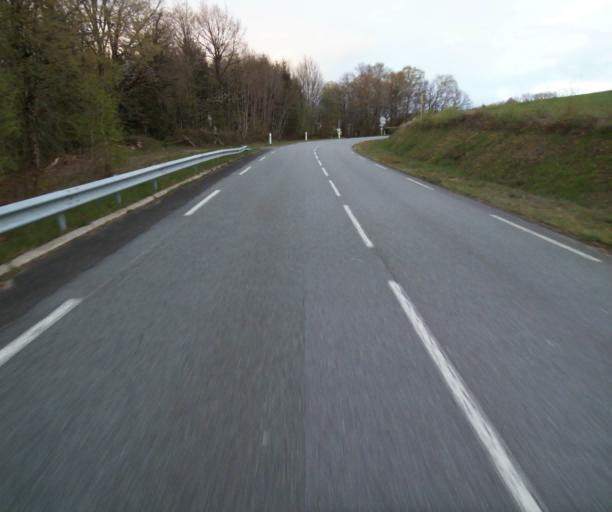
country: FR
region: Limousin
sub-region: Departement de la Correze
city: Laguenne
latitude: 45.2862
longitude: 1.8465
